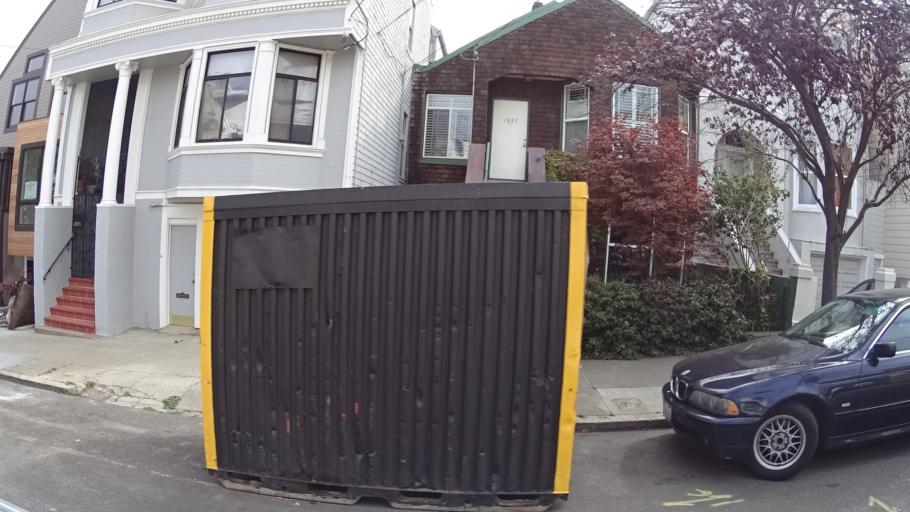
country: US
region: California
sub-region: San Francisco County
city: San Francisco
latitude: 37.7412
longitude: -122.4268
